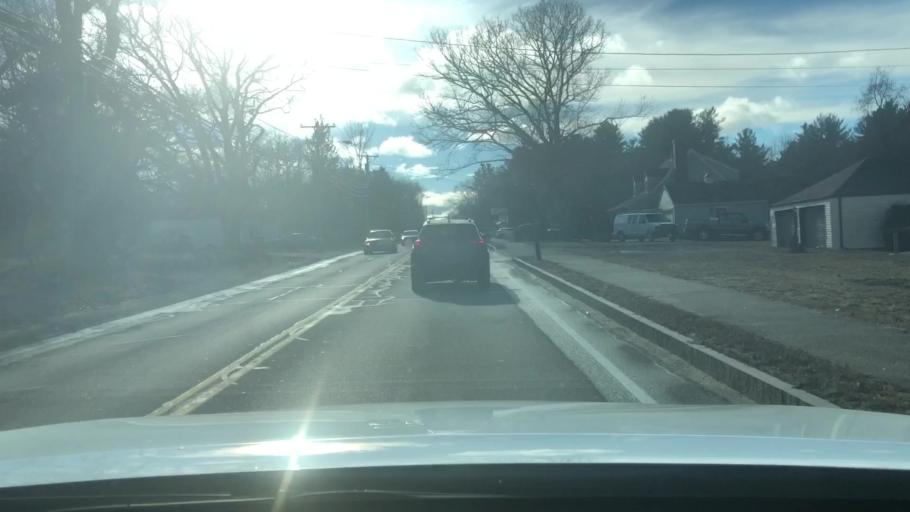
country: US
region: Massachusetts
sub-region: Norfolk County
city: Bellingham
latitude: 42.0589
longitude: -71.4854
